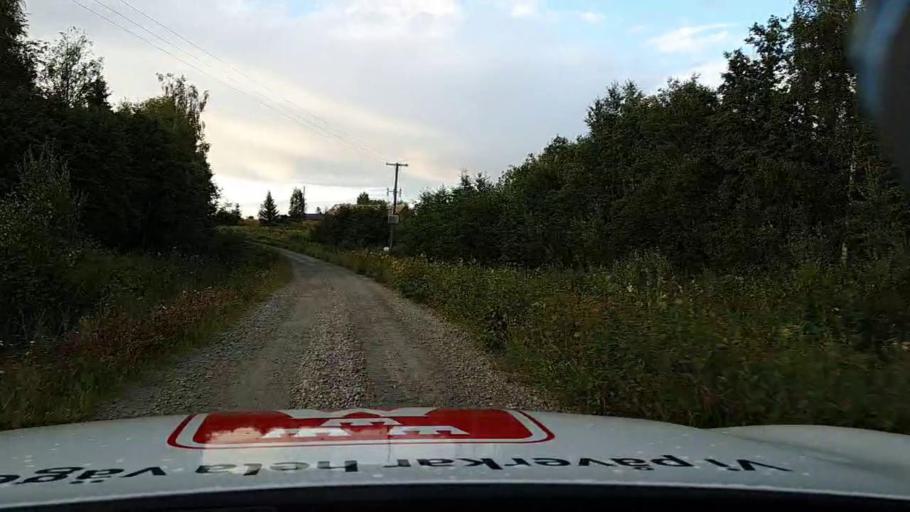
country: SE
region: Jaemtland
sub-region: Bergs Kommun
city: Hoverberg
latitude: 62.8701
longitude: 14.6214
